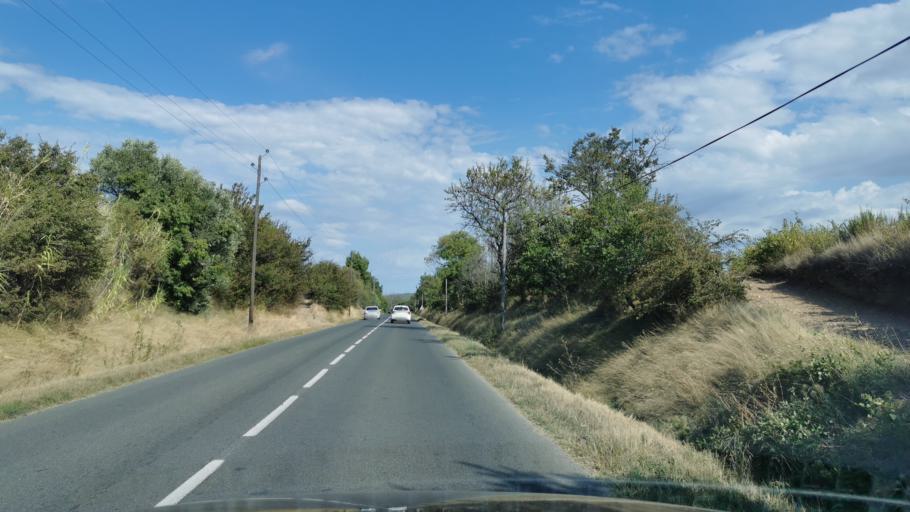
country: FR
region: Languedoc-Roussillon
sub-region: Departement de l'Aude
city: Azille
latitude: 43.2491
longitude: 2.6648
